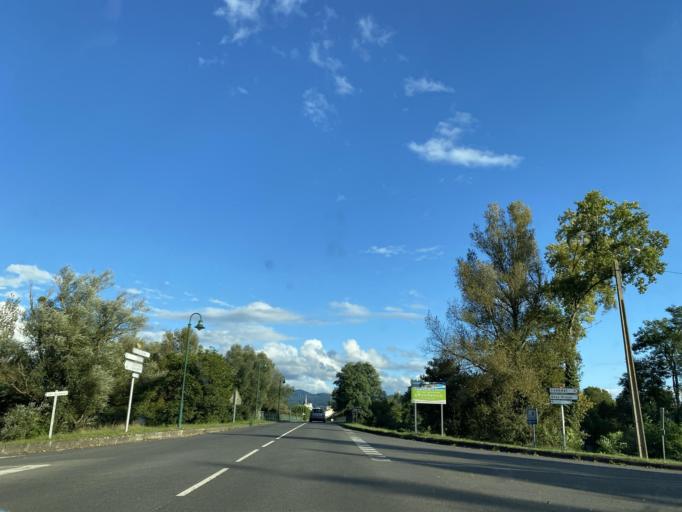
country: FR
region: Auvergne
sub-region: Departement du Puy-de-Dome
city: Puy-Guillaume
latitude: 45.9631
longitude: 3.4630
